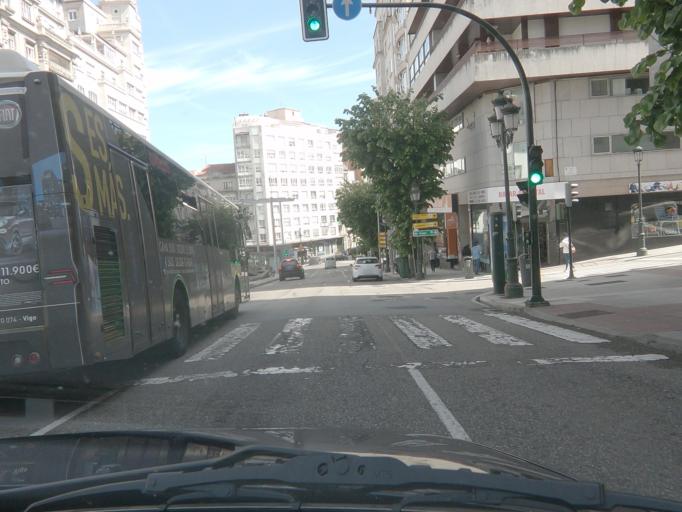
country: ES
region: Galicia
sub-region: Provincia de Pontevedra
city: Vigo
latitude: 42.2333
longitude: -8.7128
